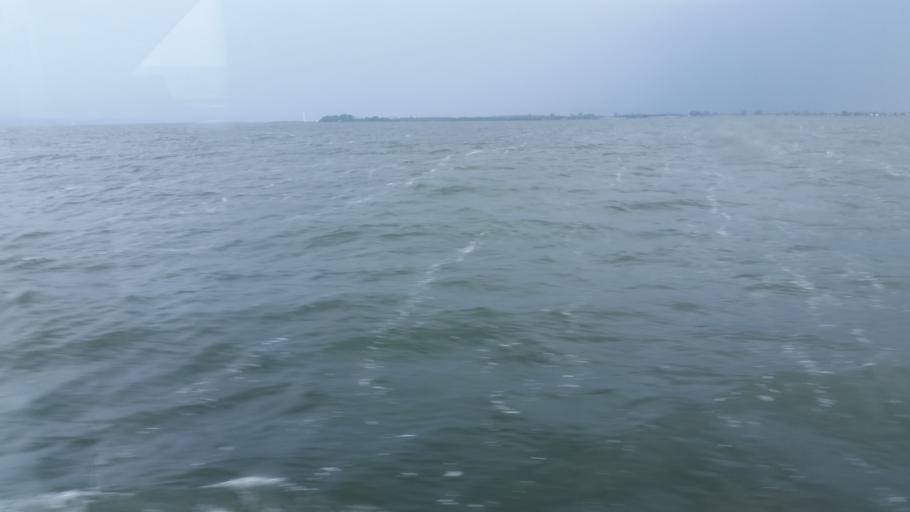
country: DE
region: Mecklenburg-Vorpommern
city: Hiddensee
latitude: 54.5244
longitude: 13.1357
